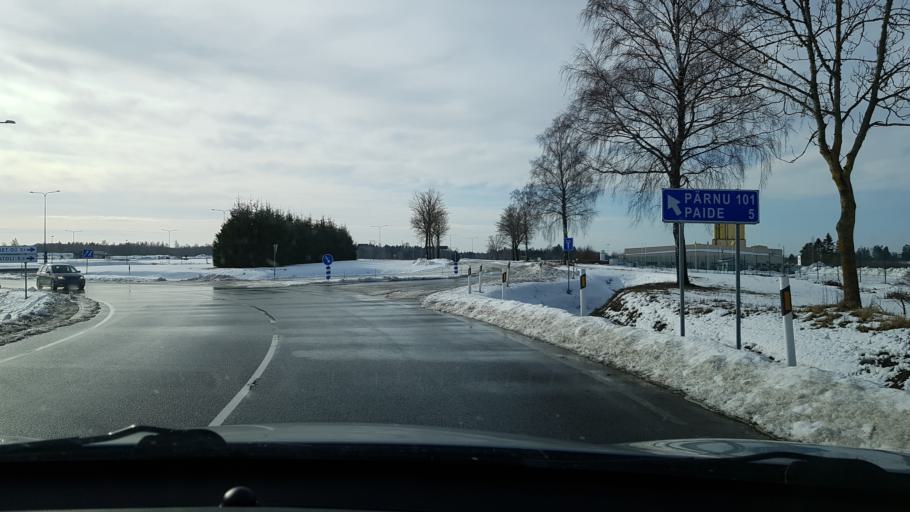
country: EE
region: Jaervamaa
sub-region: Paide linn
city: Paide
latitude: 58.9170
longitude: 25.6088
